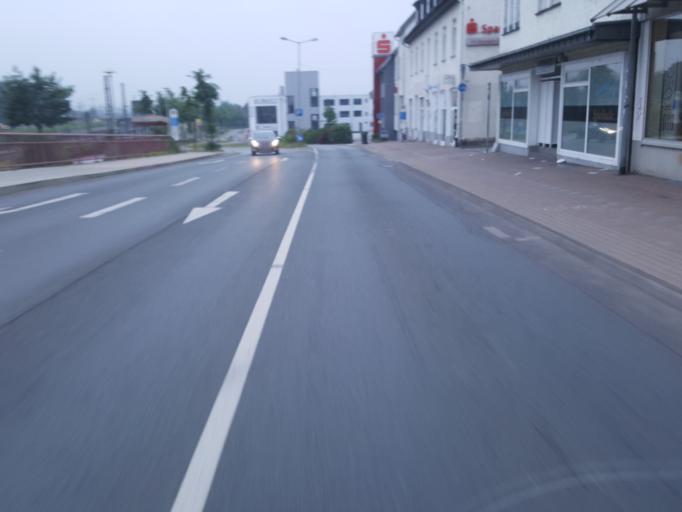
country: DE
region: North Rhine-Westphalia
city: Loehne
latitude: 52.1982
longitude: 8.7193
